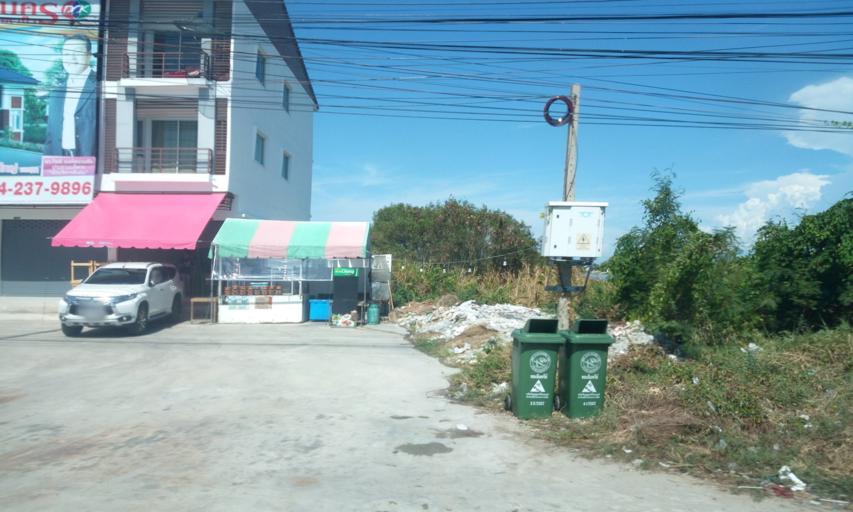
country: TH
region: Samut Prakan
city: Bang Bo District
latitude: 13.5296
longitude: 100.7883
